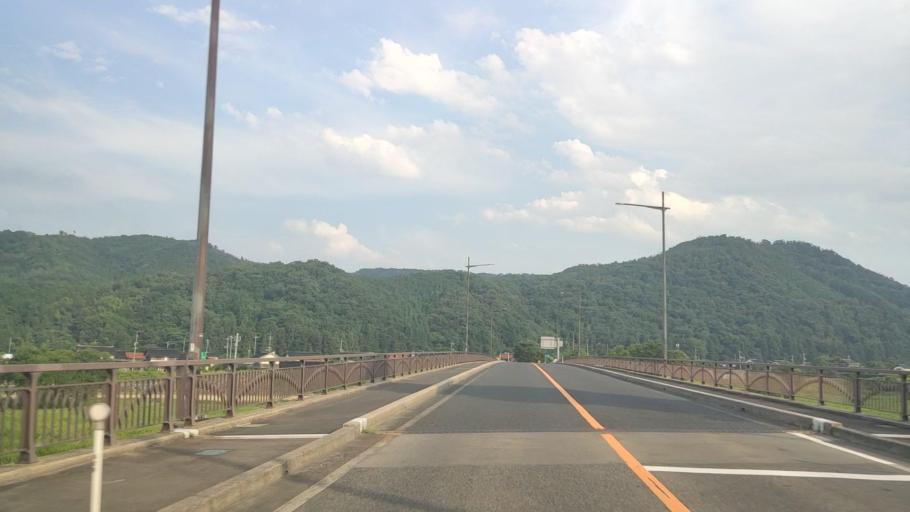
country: JP
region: Tottori
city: Kurayoshi
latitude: 35.3900
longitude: 133.7797
